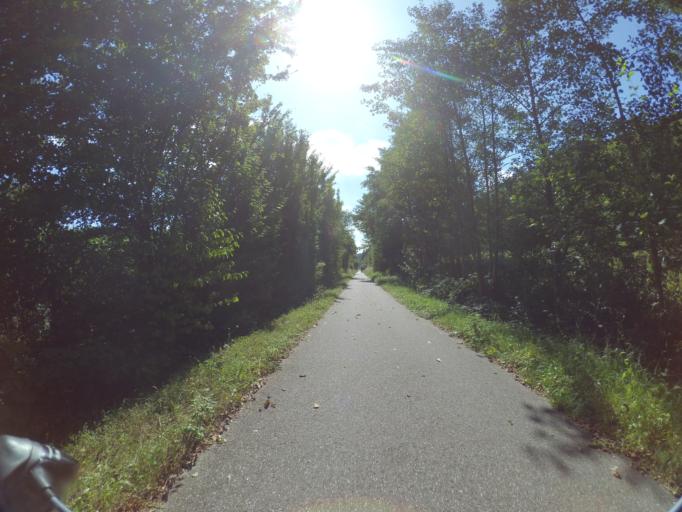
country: DE
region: Rheinland-Pfalz
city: Mertesdorf
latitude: 49.7764
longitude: 6.7160
